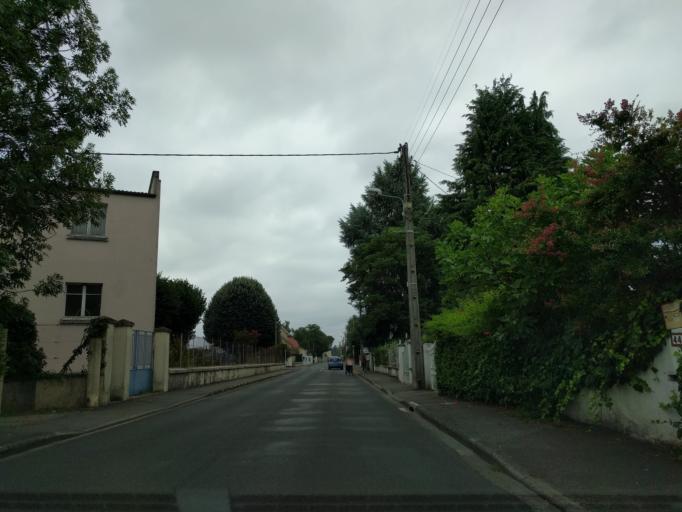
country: FR
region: Midi-Pyrenees
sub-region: Departement des Hautes-Pyrenees
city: Tarbes
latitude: 43.2255
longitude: 0.0628
